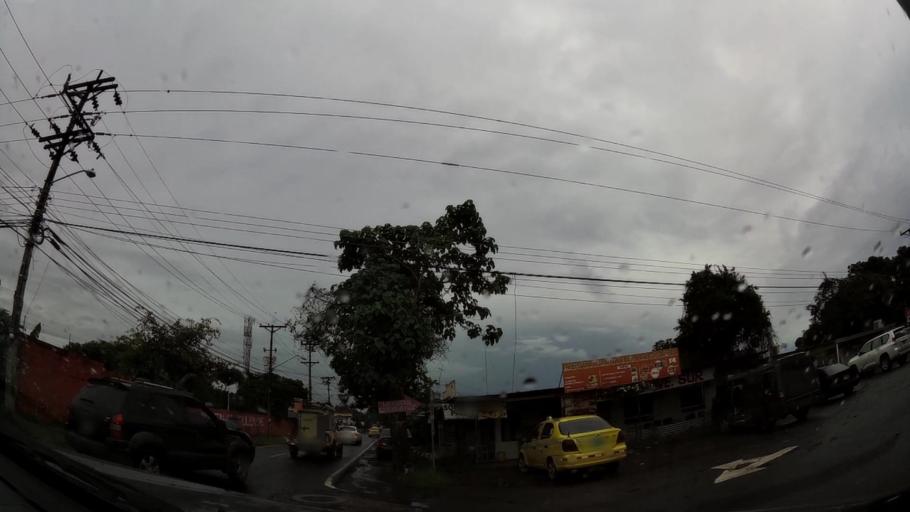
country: PA
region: Veraguas
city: Santiago de Veraguas
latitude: 8.0958
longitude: -80.9802
